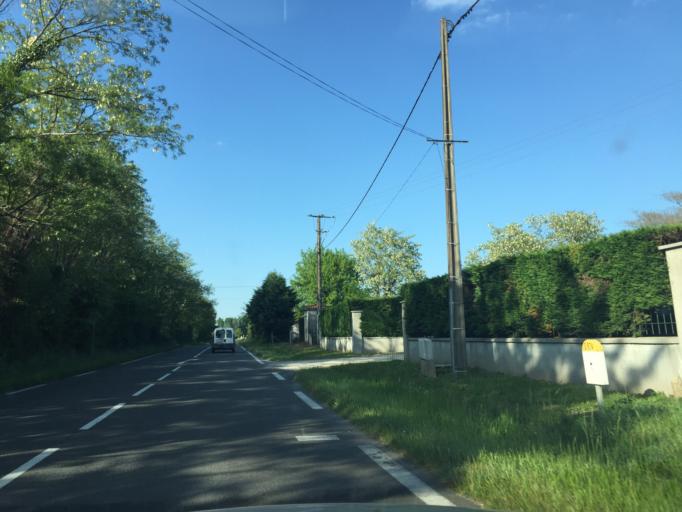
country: FR
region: Aquitaine
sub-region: Departement de la Gironde
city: Les Eglisottes-et-Chalaures
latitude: 45.1111
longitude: -0.0156
